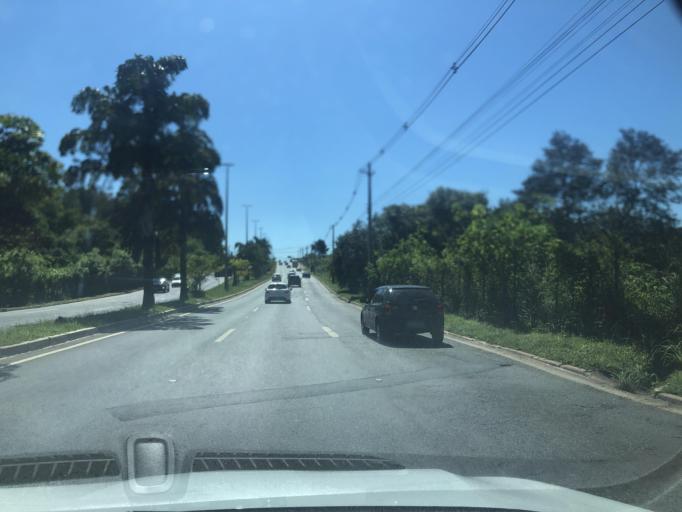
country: BR
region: Federal District
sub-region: Brasilia
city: Brasilia
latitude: -15.8373
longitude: -47.9594
